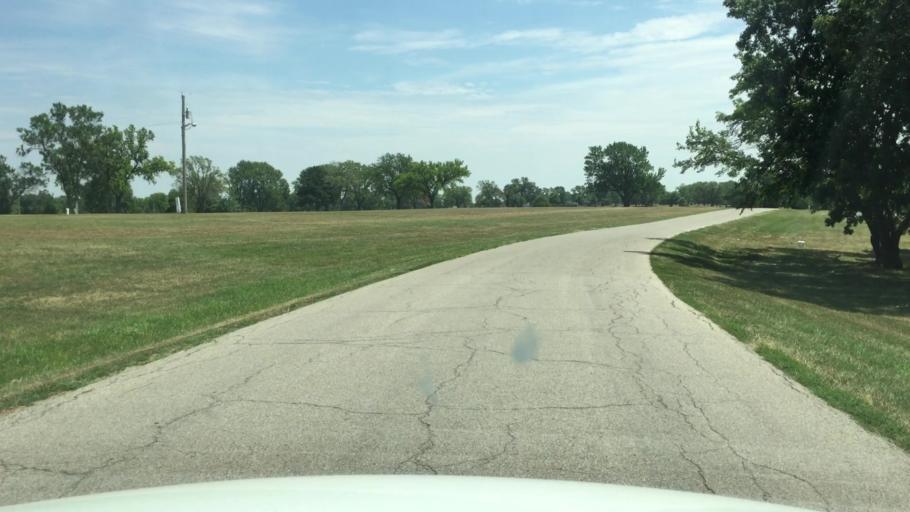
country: US
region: Kansas
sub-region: Shawnee County
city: Topeka
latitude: 39.0087
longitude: -95.6220
